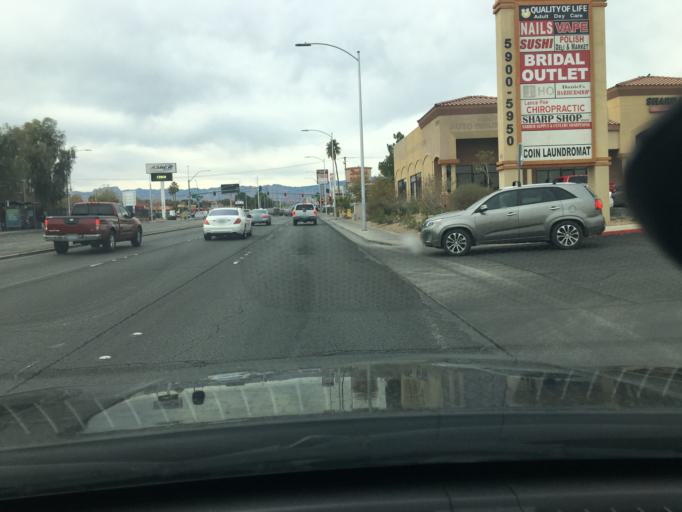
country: US
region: Nevada
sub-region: Clark County
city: Spring Valley
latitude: 36.1593
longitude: -115.2222
